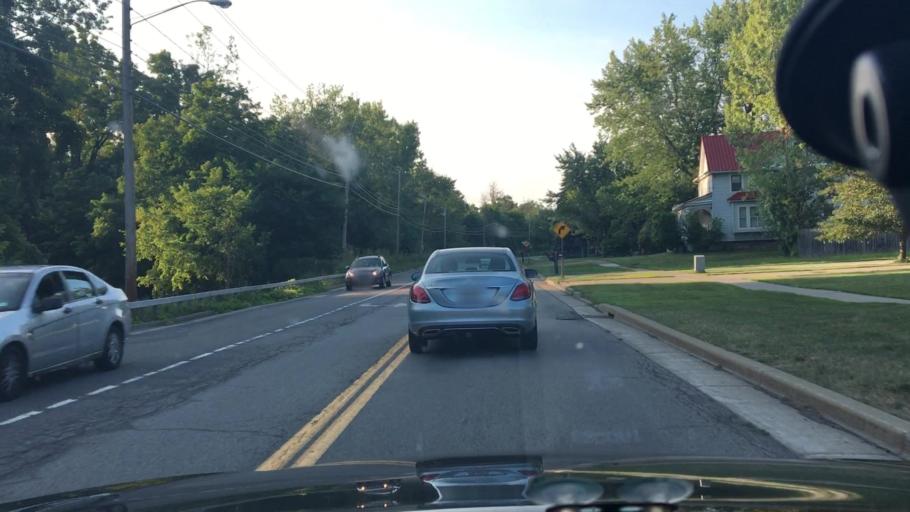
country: US
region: New York
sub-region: Erie County
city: Williamsville
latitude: 42.9974
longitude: -78.7605
